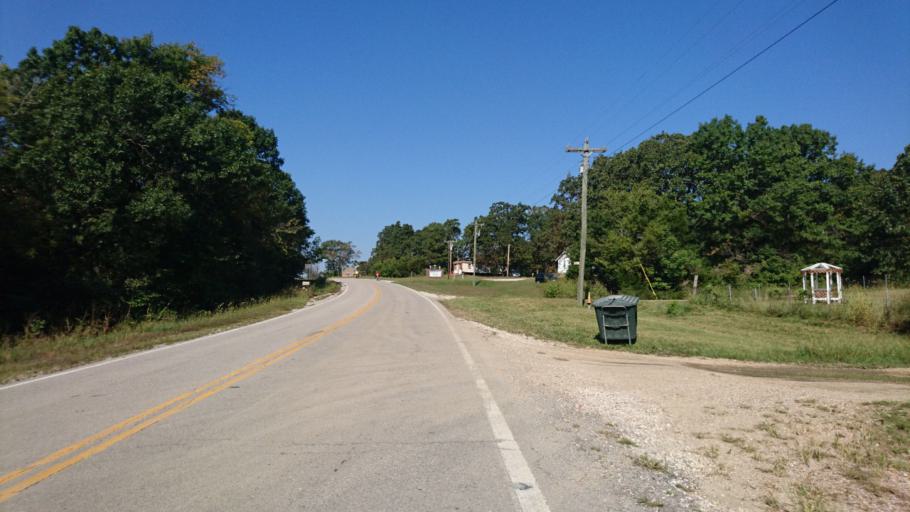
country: US
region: Missouri
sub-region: Pulaski County
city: Richland
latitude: 37.7669
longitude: -92.4020
